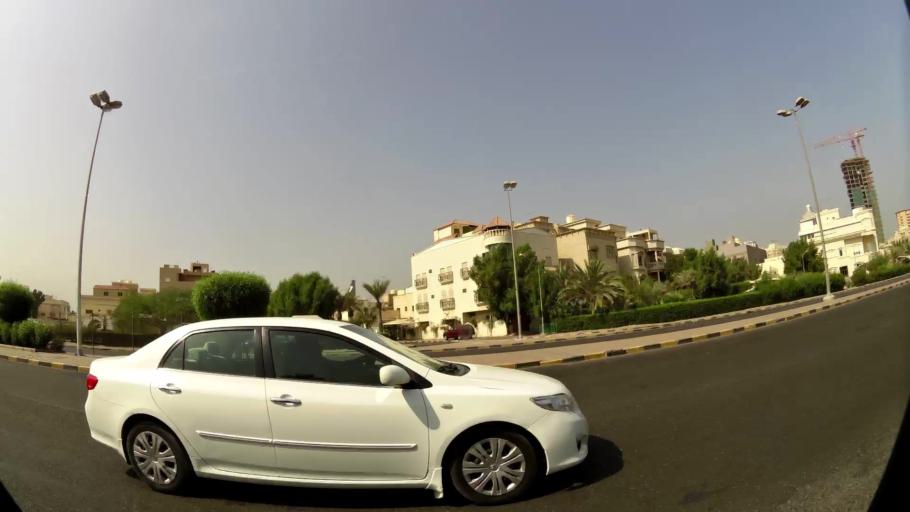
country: KW
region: Al Asimah
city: Ad Dasmah
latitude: 29.3633
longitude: 48.0093
